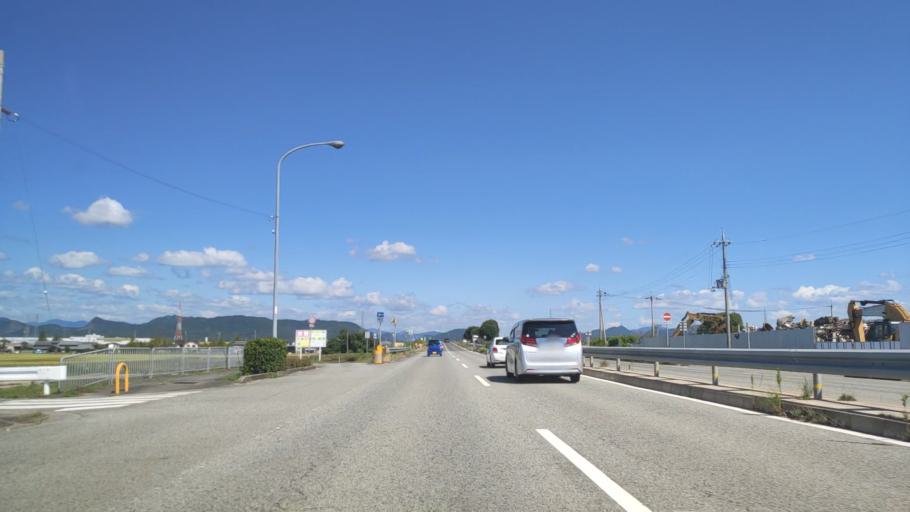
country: JP
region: Hyogo
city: Yashiro
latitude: 34.9017
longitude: 134.9521
